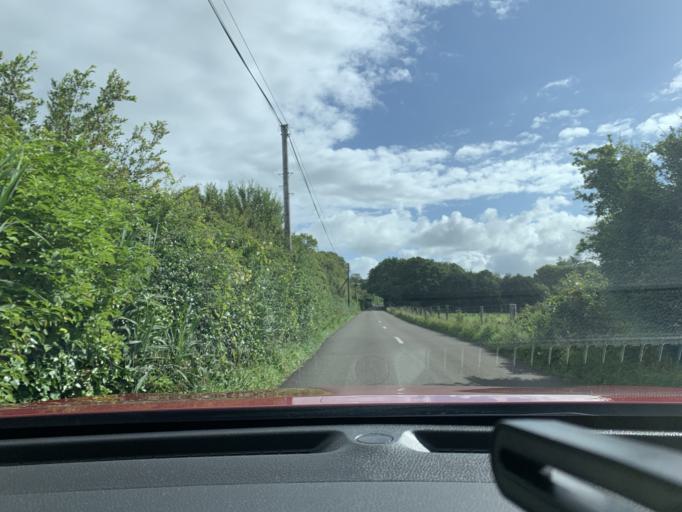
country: IE
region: Connaught
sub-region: Sligo
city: Strandhill
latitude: 54.3567
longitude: -8.5938
